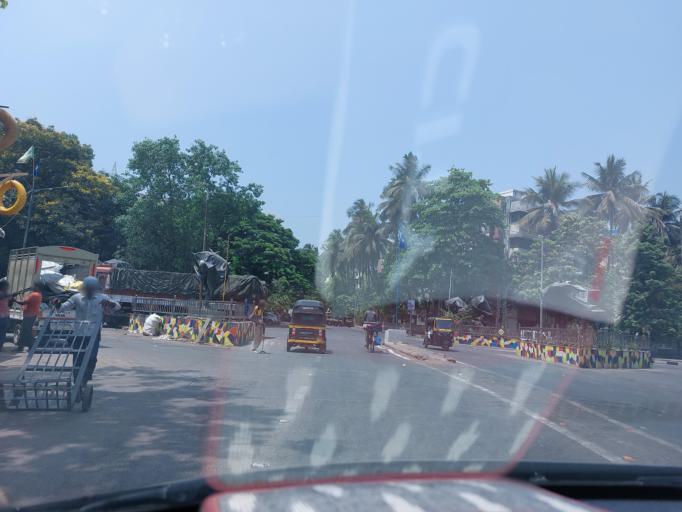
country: IN
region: Maharashtra
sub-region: Mumbai Suburban
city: Mumbai
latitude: 19.0566
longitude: 72.8840
